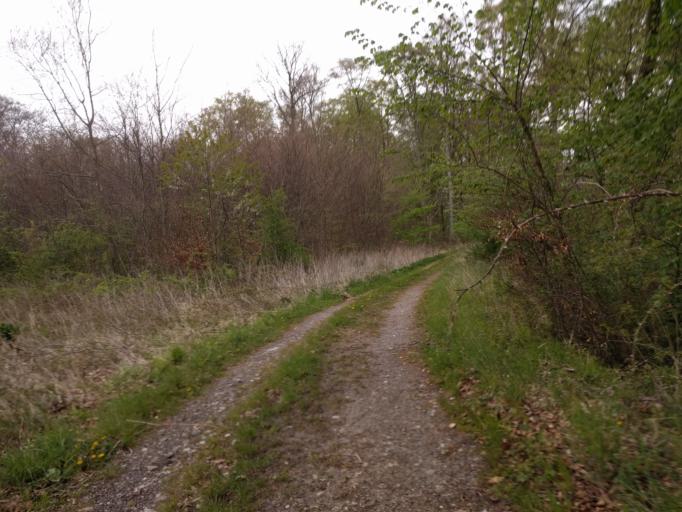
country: DK
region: South Denmark
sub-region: Kerteminde Kommune
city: Munkebo
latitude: 55.4243
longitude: 10.5507
